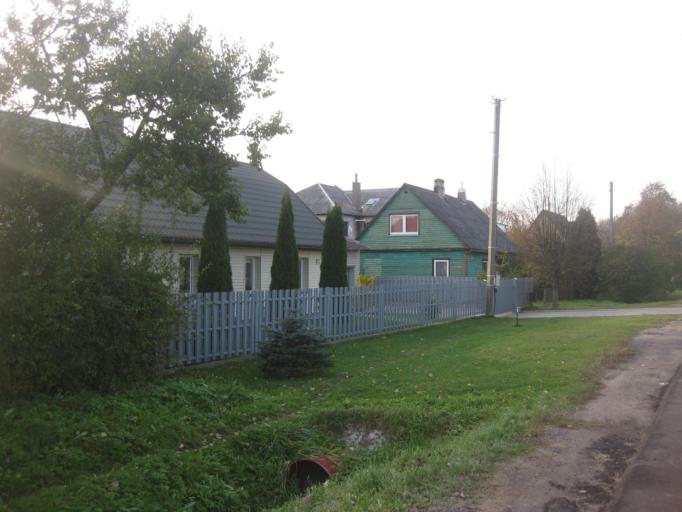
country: LT
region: Kauno apskritis
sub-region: Kaunas
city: Kaunas
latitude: 54.8924
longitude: 23.8719
